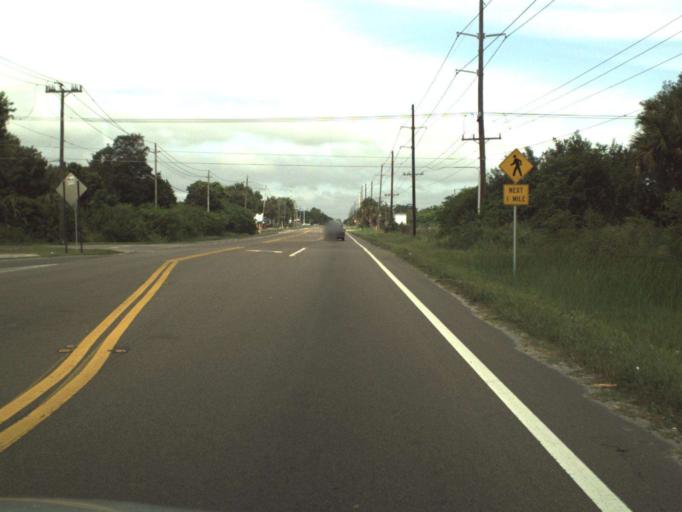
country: US
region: Florida
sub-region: Seminole County
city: Midway
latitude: 28.7869
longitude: -81.2138
